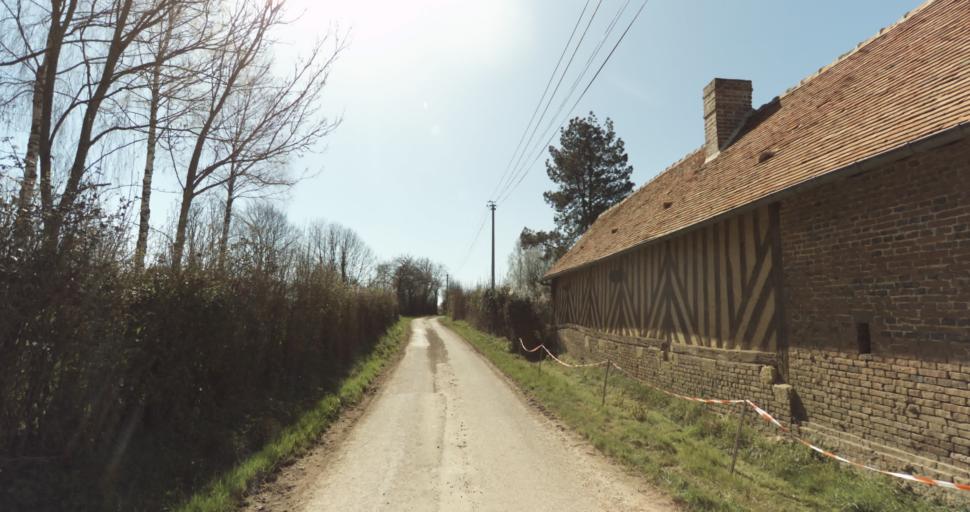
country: FR
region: Lower Normandy
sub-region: Departement du Calvados
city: Livarot
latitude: 49.0177
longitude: 0.1042
